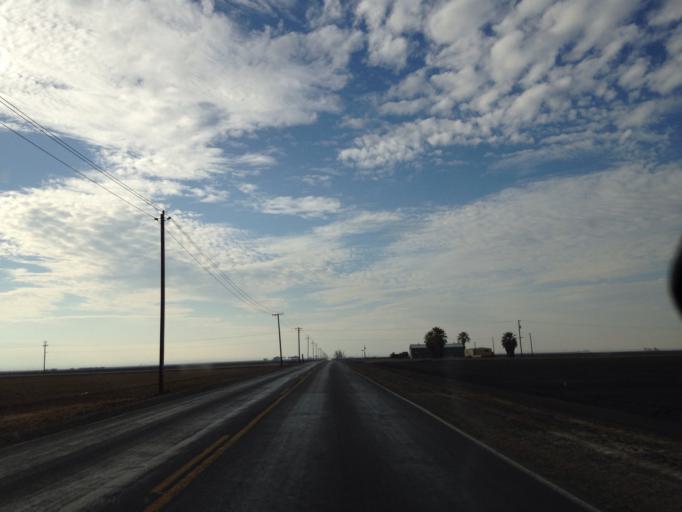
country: US
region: California
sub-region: Kern County
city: Buttonwillow
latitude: 35.4422
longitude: -119.5151
